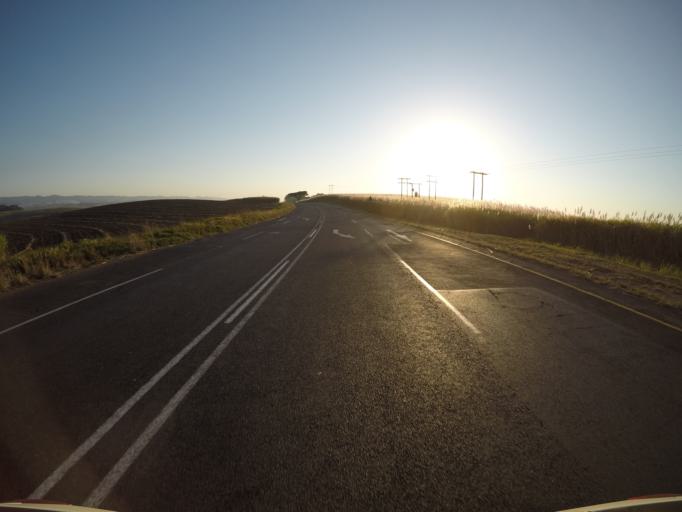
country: ZA
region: KwaZulu-Natal
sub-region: uThungulu District Municipality
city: eSikhawini
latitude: -28.9412
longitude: 31.7391
